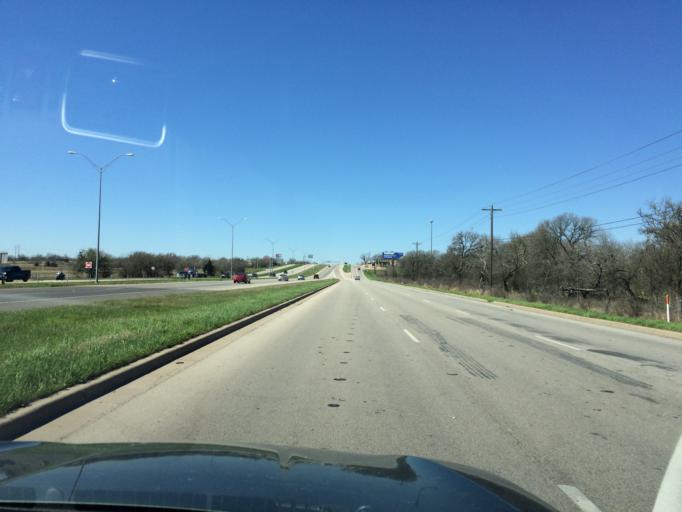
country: US
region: Texas
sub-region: Bastrop County
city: Bastrop
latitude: 30.1114
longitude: -97.3589
